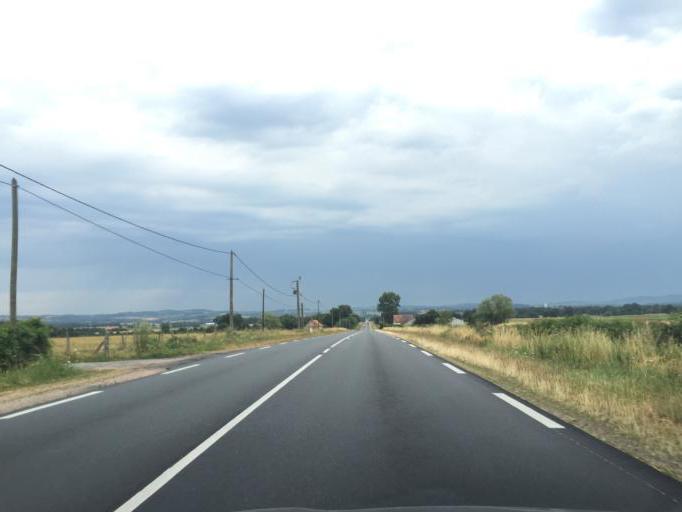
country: FR
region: Auvergne
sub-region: Departement de l'Allier
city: Saint-Gerand-le-Puy
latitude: 46.2495
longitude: 3.5705
